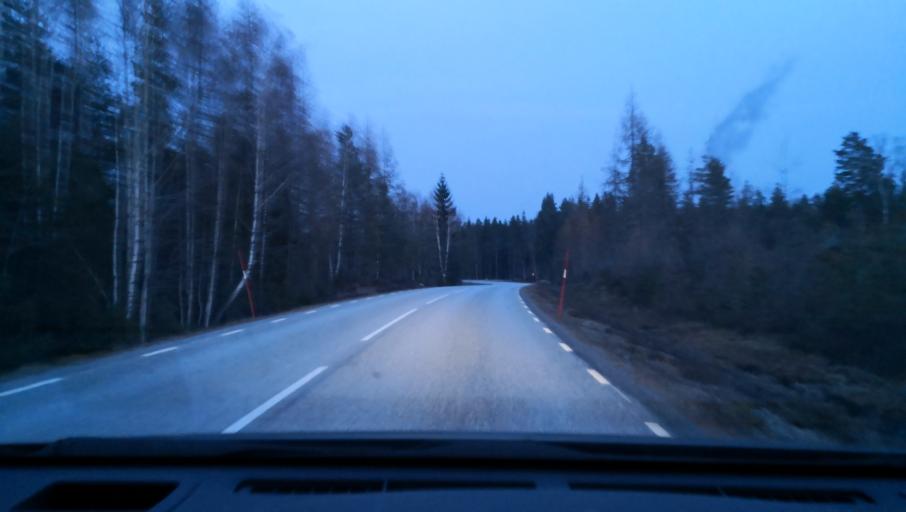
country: SE
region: OErebro
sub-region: Lindesbergs Kommun
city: Frovi
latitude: 59.5922
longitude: 15.4017
